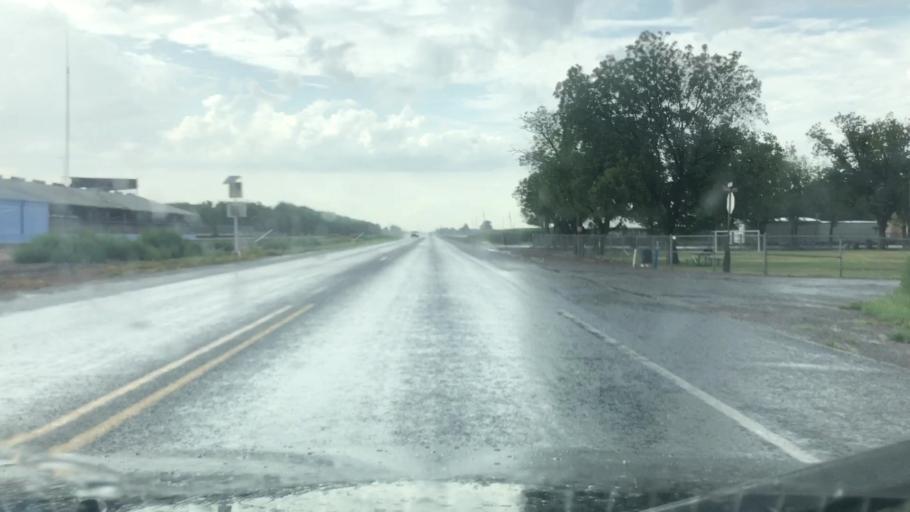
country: US
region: New Mexico
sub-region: Dona Ana County
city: Mesquite
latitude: 32.1667
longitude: -106.6979
